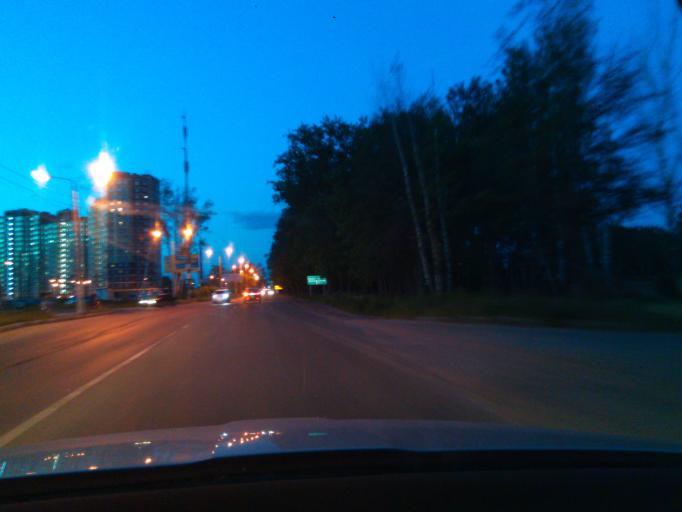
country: RU
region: Moskovskaya
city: Dolgoprudnyy
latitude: 55.9593
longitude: 37.5259
